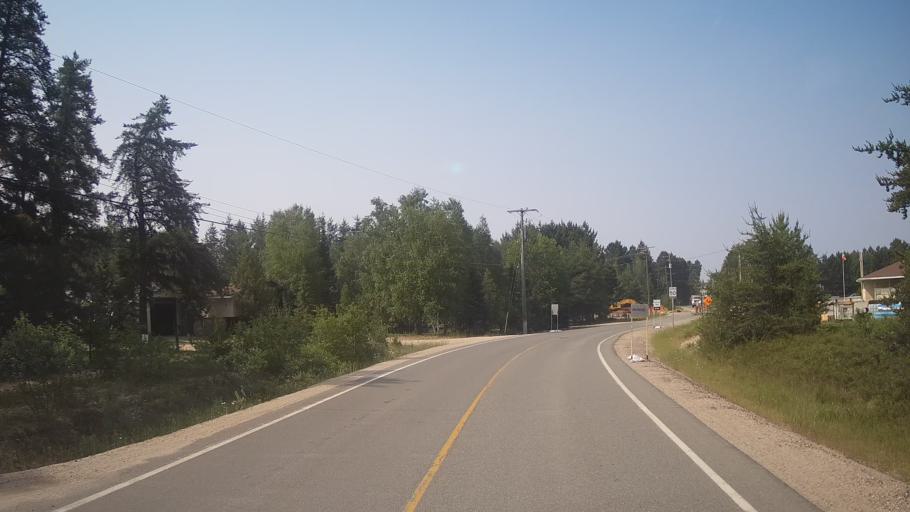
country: CA
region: Ontario
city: Timmins
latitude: 47.6781
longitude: -81.7165
